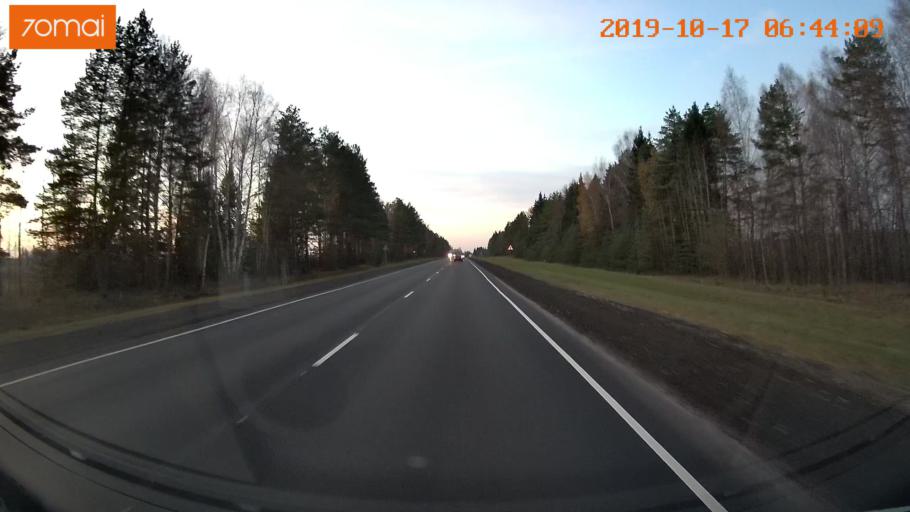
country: RU
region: Vladimir
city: Kideksha
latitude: 56.5768
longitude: 40.5547
